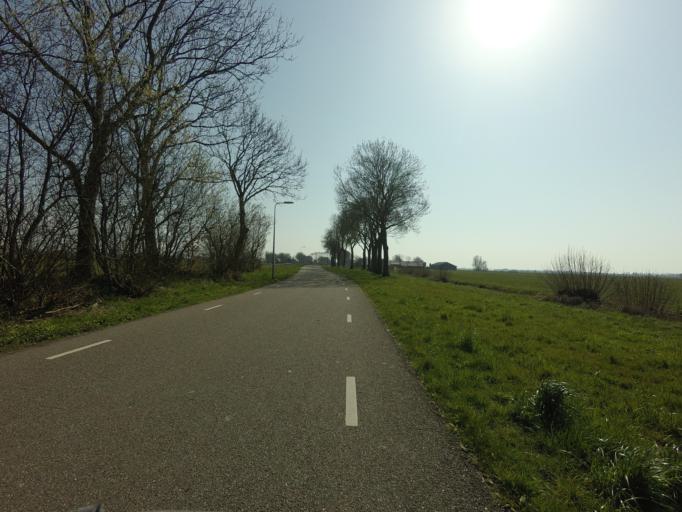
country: NL
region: South Holland
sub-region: Gemeente Vlist
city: Vlist
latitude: 52.0028
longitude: 4.8149
